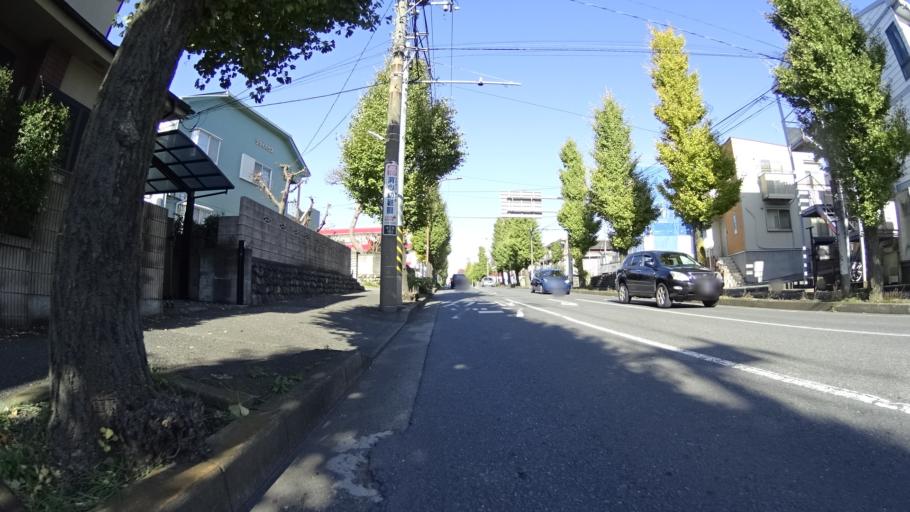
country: JP
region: Tokyo
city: Hachioji
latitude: 35.5751
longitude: 139.3601
